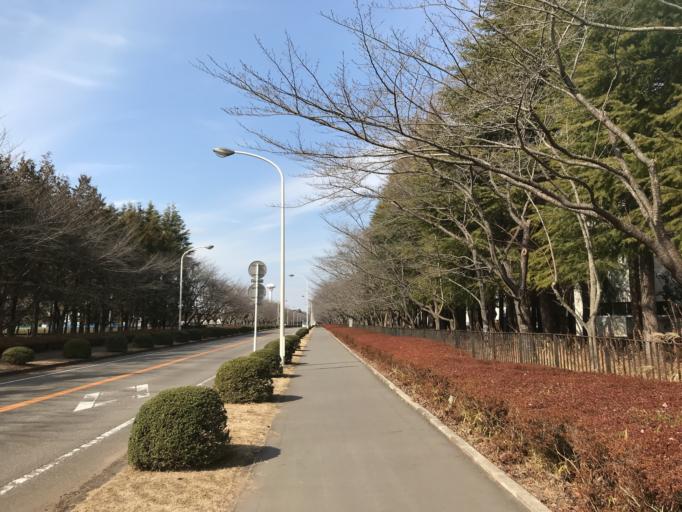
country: JP
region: Ibaraki
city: Naka
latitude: 36.0270
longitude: 140.1088
